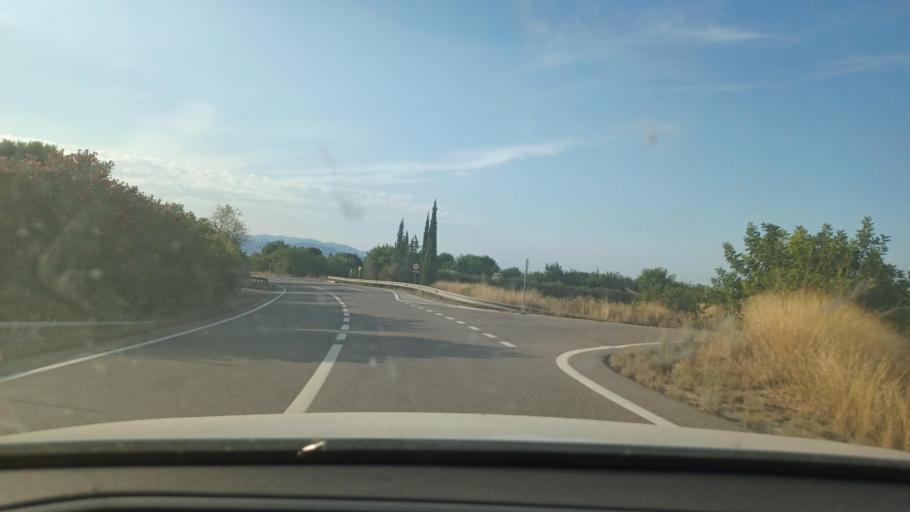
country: ES
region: Catalonia
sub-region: Provincia de Tarragona
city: Santa Barbara
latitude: 40.7129
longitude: 0.4845
